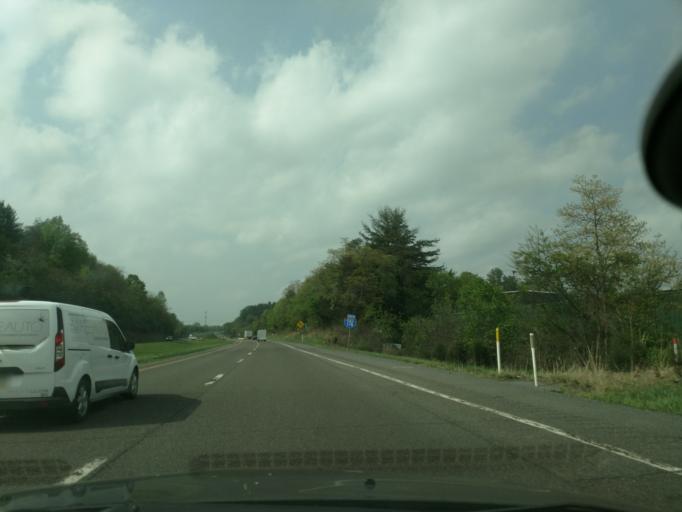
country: US
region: Pennsylvania
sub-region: Berks County
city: Flying Hills
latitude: 40.2565
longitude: -75.9134
